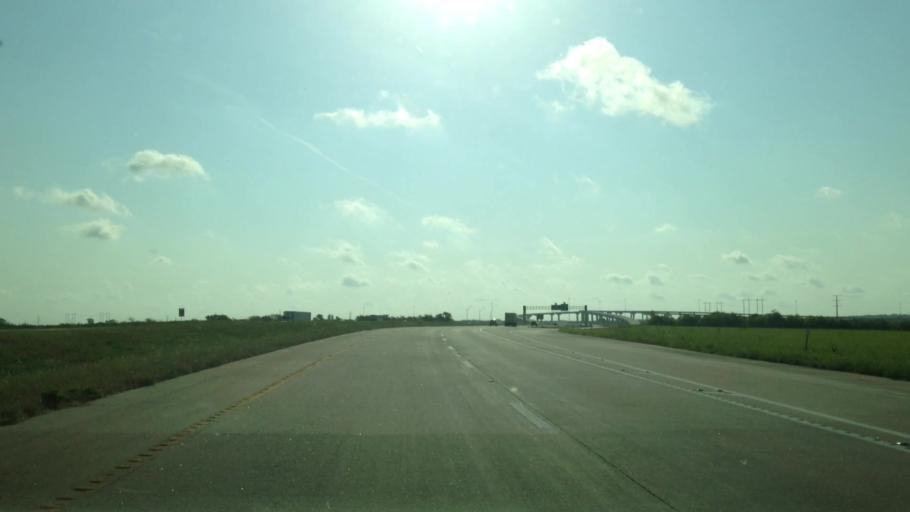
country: US
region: Texas
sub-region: Travis County
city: Onion Creek
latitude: 30.0820
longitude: -97.7118
